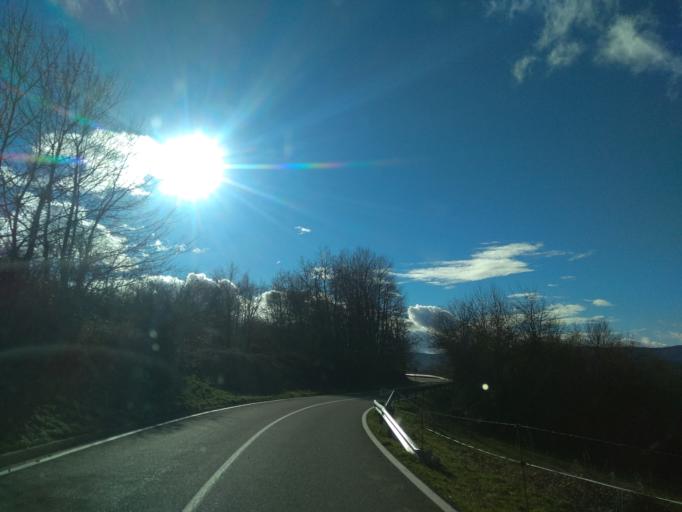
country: ES
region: Cantabria
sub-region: Provincia de Cantabria
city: San Martin de Elines
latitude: 42.9187
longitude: -3.8639
